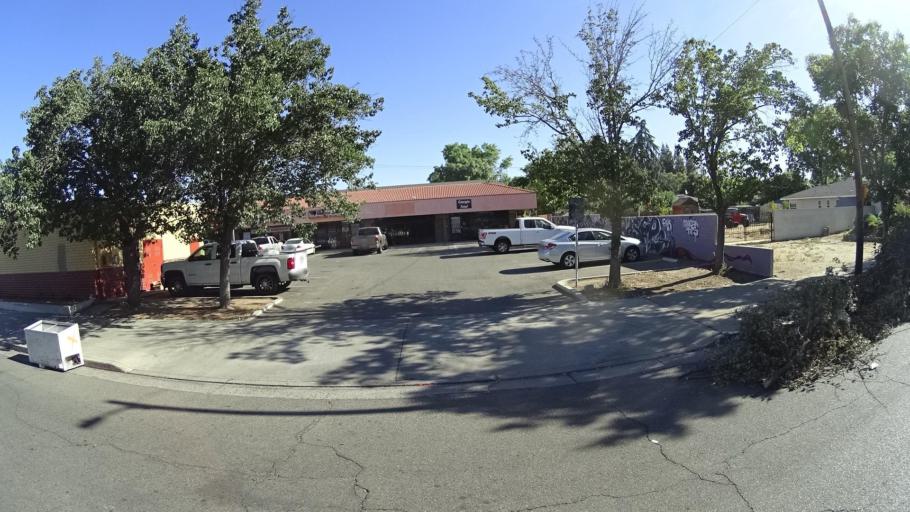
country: US
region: California
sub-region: Fresno County
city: Fresno
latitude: 36.7696
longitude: -119.7901
